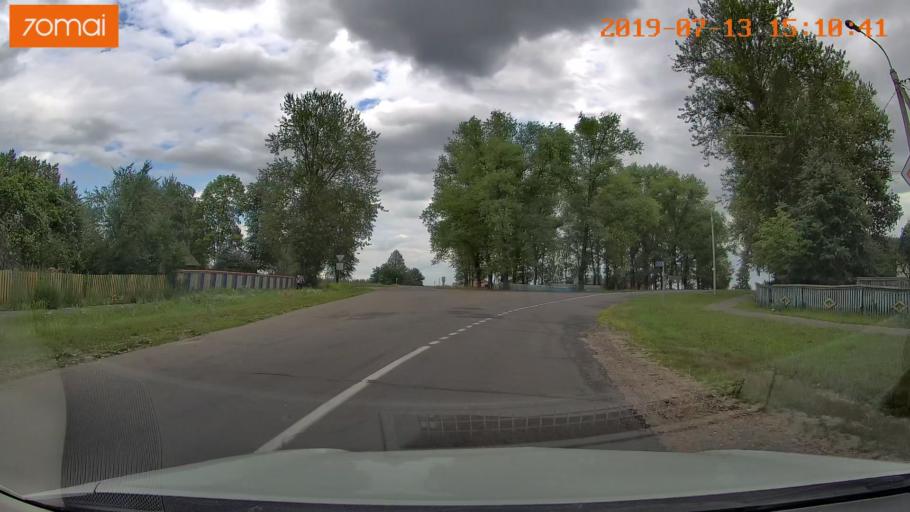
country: BY
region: Mogilev
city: Hlusha
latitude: 53.1693
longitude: 28.7779
